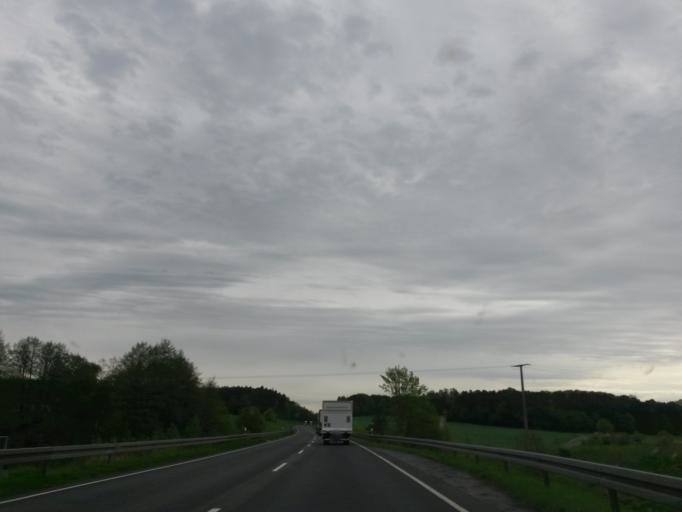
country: DE
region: Bavaria
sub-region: Regierungsbezirk Mittelfranken
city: Adelsdorf
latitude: 49.7617
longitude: 10.8730
